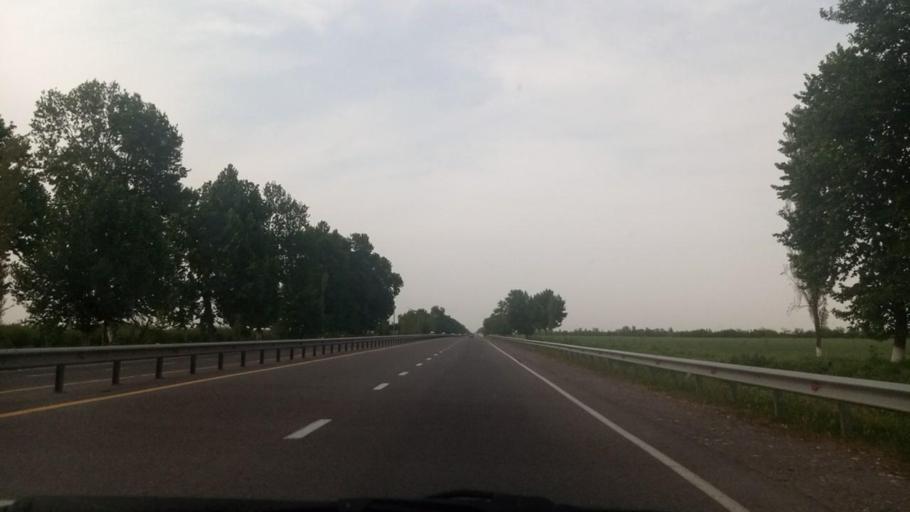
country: UZ
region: Toshkent Shahri
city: Bektemir
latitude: 41.1940
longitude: 69.4032
